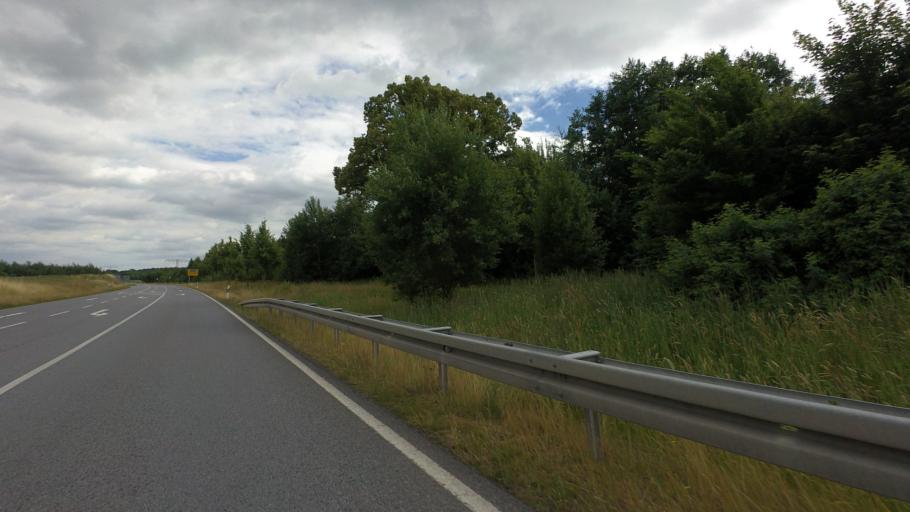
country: DE
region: Saxony
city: Nebelschutz
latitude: 51.2649
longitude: 14.1453
